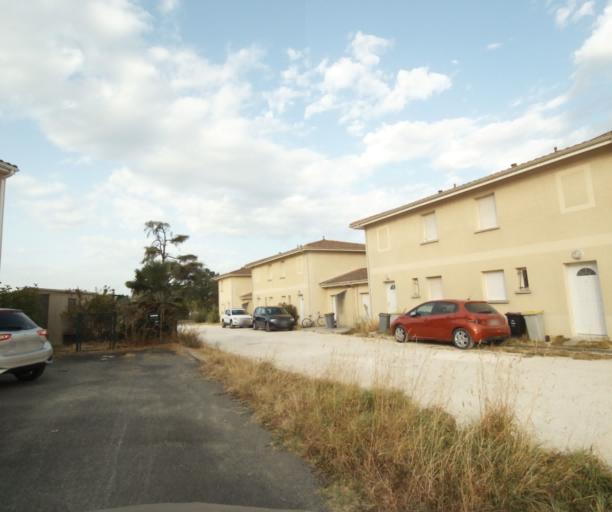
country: FR
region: Aquitaine
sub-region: Departement de la Gironde
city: Creon
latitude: 44.7771
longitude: -0.3480
